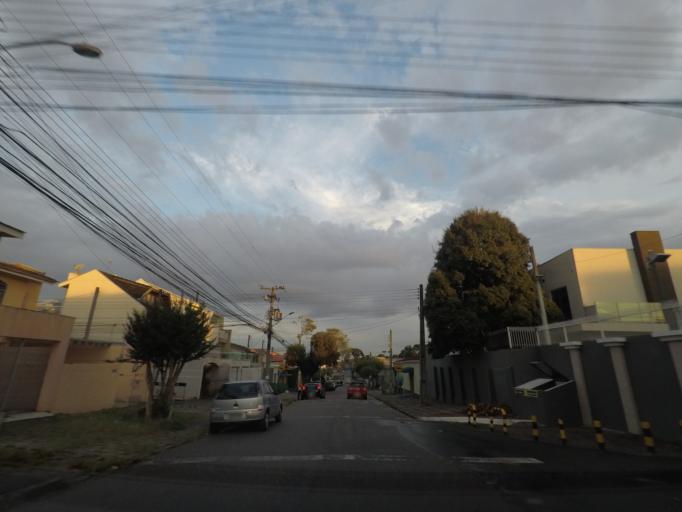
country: BR
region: Parana
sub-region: Sao Jose Dos Pinhais
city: Sao Jose dos Pinhais
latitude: -25.5030
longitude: -49.2518
